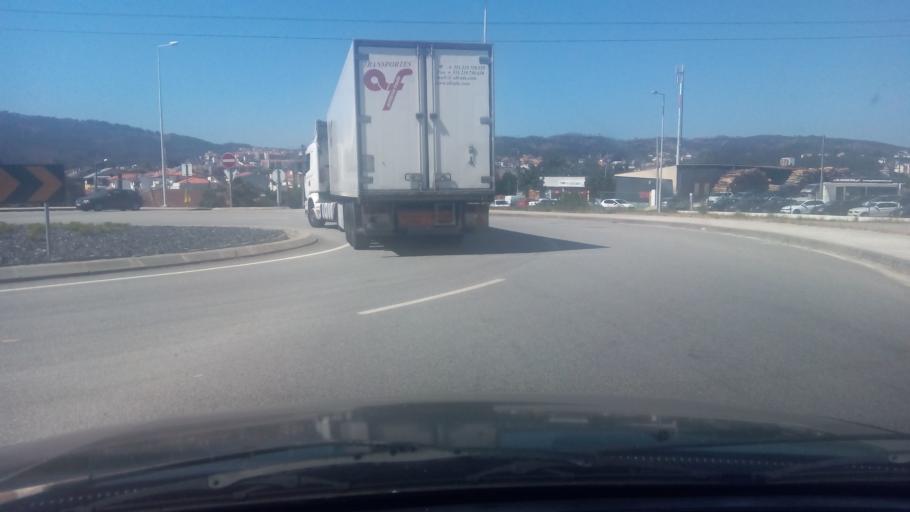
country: PT
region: Porto
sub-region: Valongo
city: Campo
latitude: 41.1850
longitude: -8.4546
